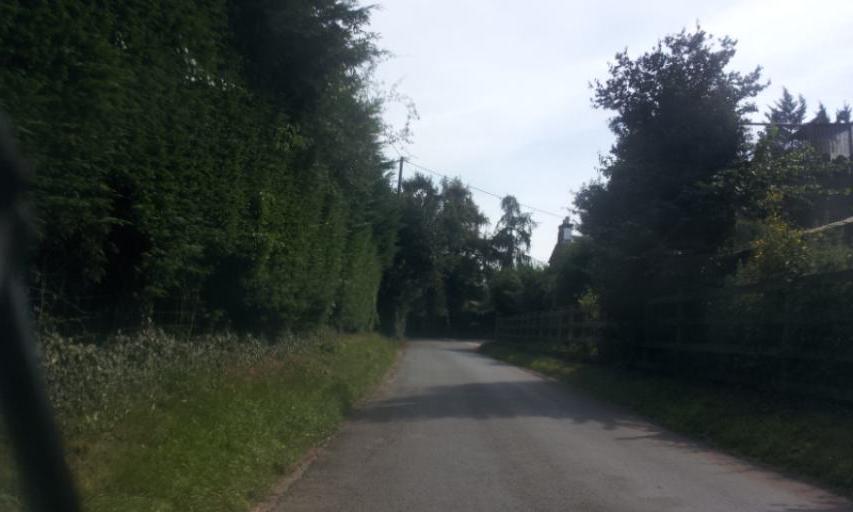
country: GB
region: England
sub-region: Kent
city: Newington
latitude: 51.3387
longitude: 0.6479
